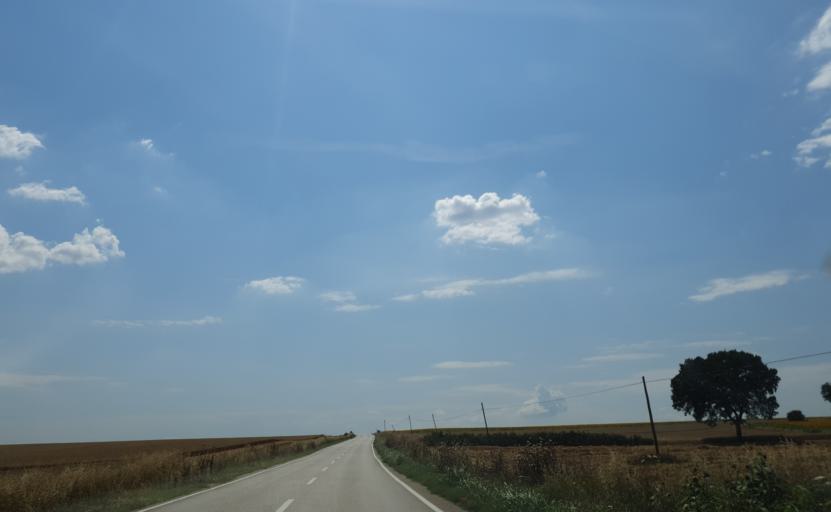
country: TR
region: Tekirdag
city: Beyazkoy
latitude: 41.4517
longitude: 27.6337
